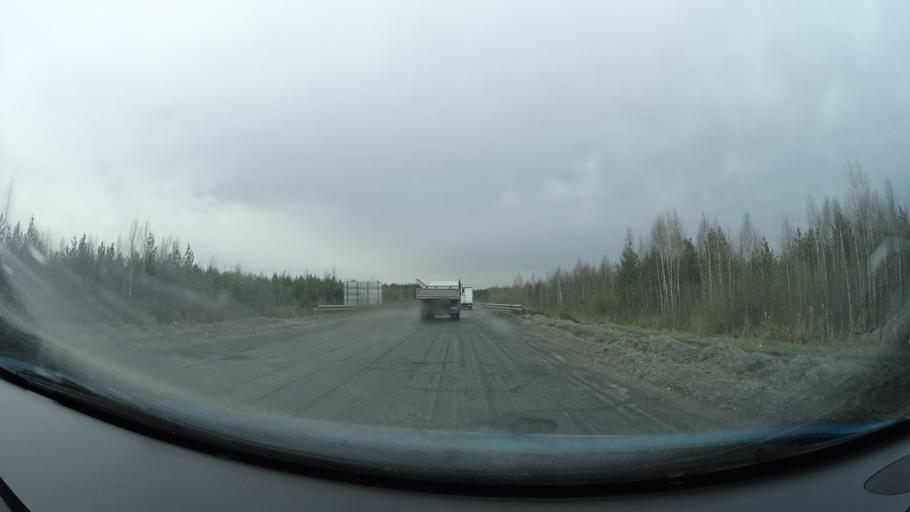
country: RU
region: Perm
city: Ust'-Kachka
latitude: 58.0844
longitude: 55.6695
